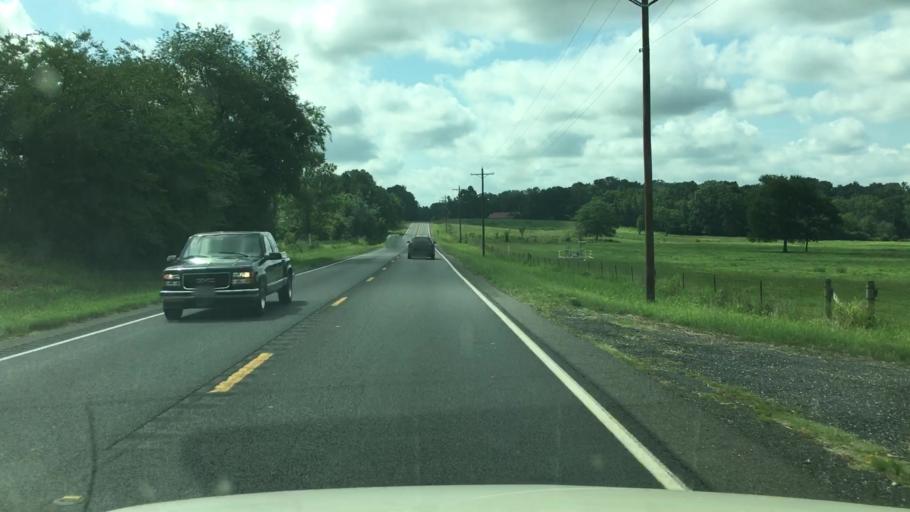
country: US
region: Arkansas
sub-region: Garland County
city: Lake Hamilton
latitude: 34.3355
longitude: -93.1787
